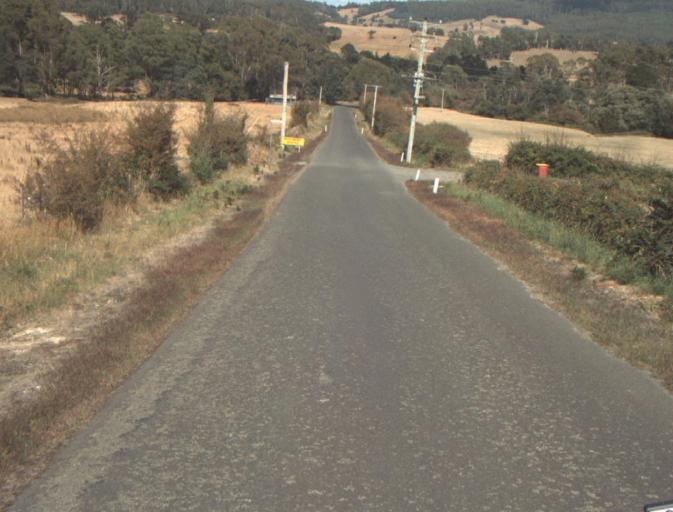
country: AU
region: Tasmania
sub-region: Launceston
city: Mayfield
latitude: -41.2593
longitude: 147.1696
